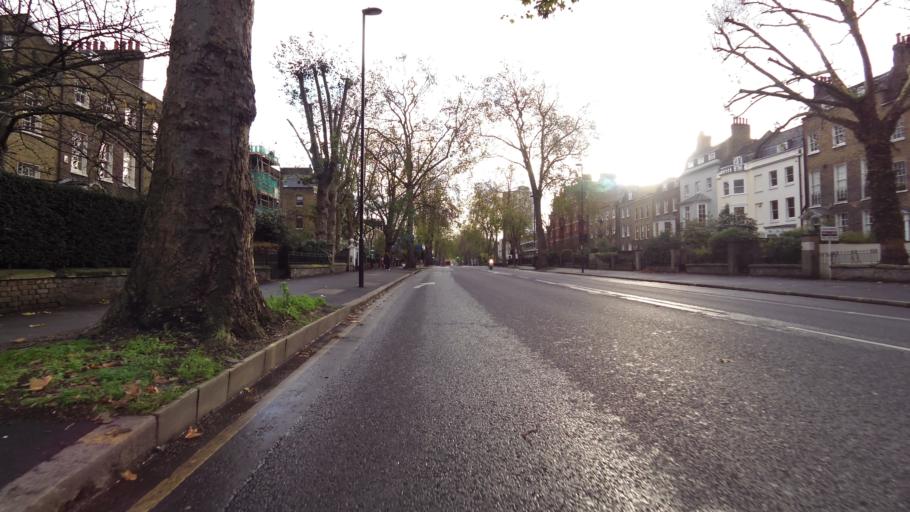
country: GB
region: England
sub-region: Greater London
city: Lambeth
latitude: 51.4945
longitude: -0.1107
